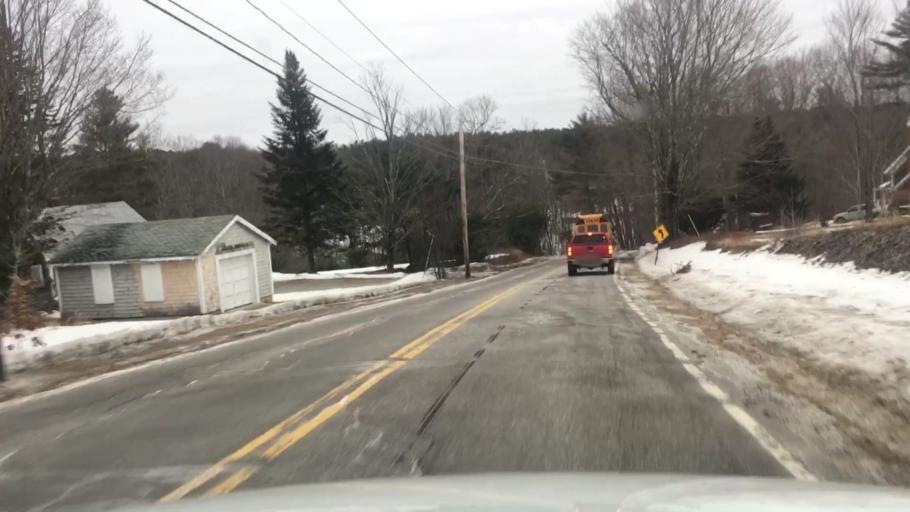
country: US
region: Maine
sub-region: York County
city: Shapleigh
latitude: 43.5384
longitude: -70.8505
